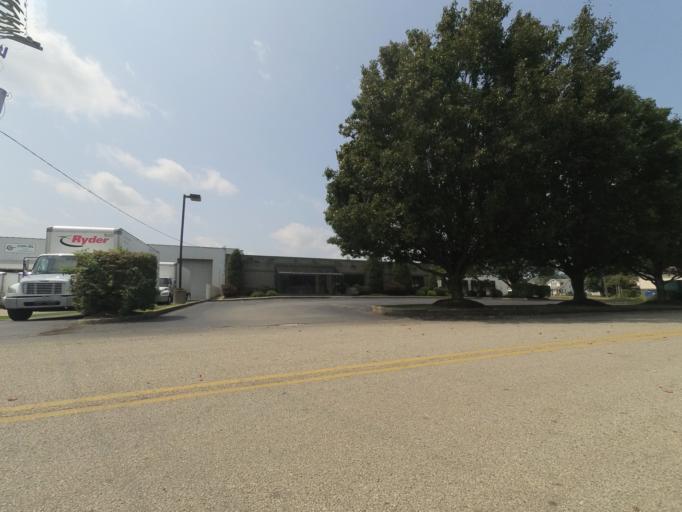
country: US
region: West Virginia
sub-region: Cabell County
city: Huntington
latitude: 38.4257
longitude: -82.4018
